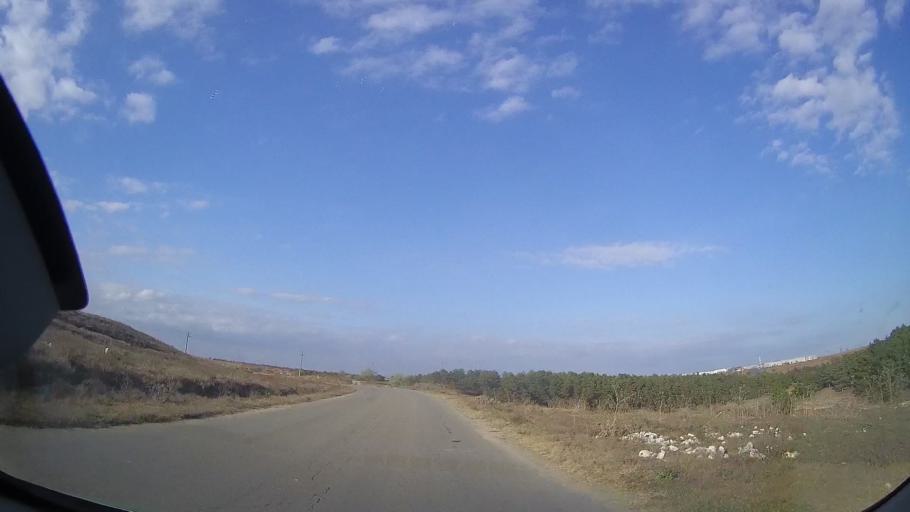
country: RO
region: Constanta
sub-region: Comuna Limanu
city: Limanu
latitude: 43.8082
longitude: 28.5201
